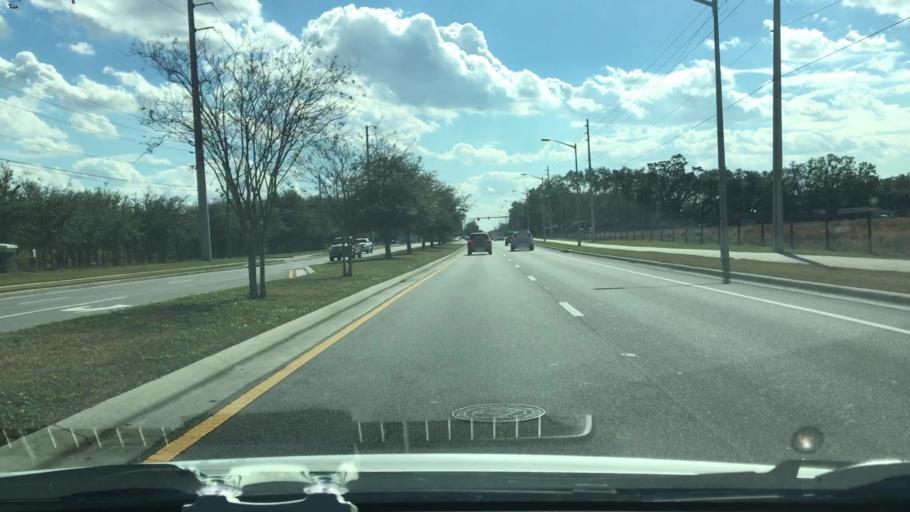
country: US
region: Florida
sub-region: Orange County
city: Conway
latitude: 28.4754
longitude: -81.3308
